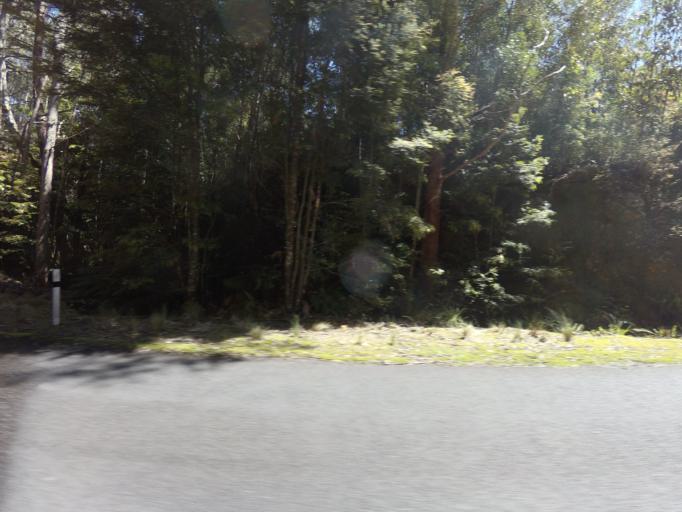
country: AU
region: Tasmania
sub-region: Huon Valley
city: Geeveston
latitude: -42.8184
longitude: 146.3443
